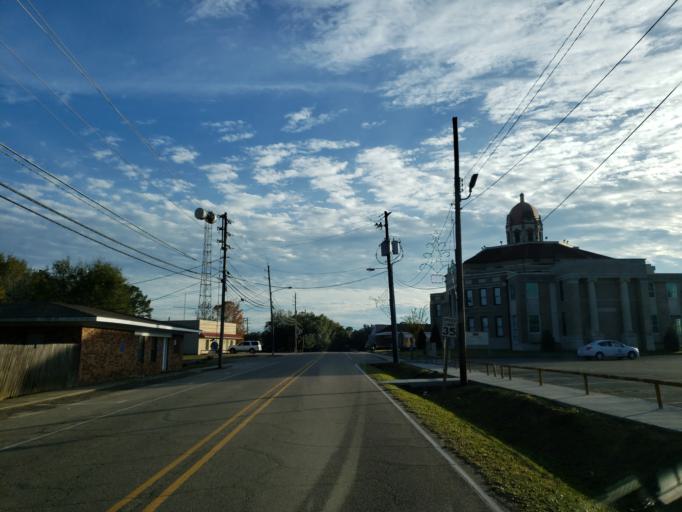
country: US
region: Mississippi
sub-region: Lamar County
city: Purvis
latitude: 31.1451
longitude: -89.4122
